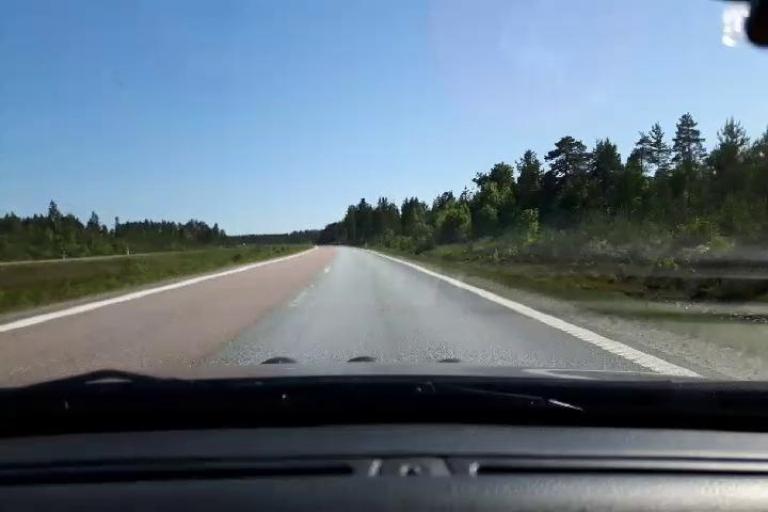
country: SE
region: Gaevleborg
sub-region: Soderhamns Kommun
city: Soderhamn
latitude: 61.3860
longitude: 16.9917
